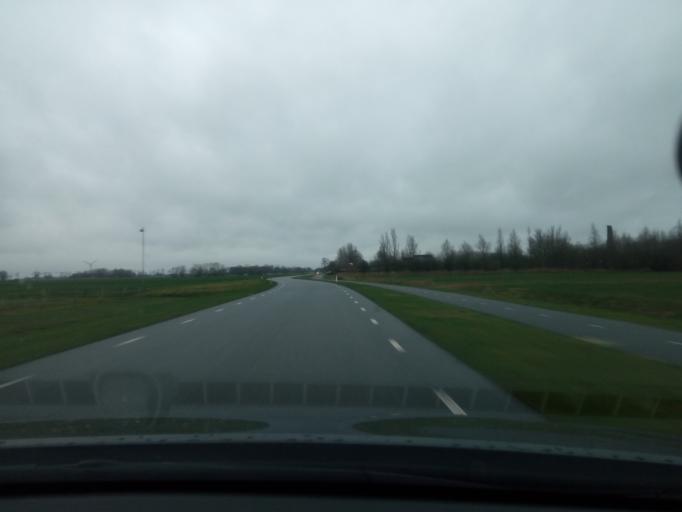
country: NL
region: Groningen
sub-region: Gemeente Winsum
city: Winsum
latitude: 53.3371
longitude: 6.5634
